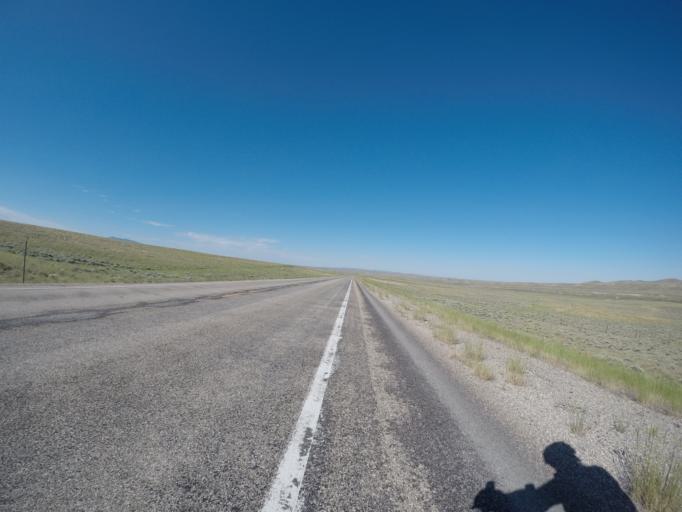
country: US
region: Wyoming
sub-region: Carbon County
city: Saratoga
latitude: 41.8824
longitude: -106.4811
